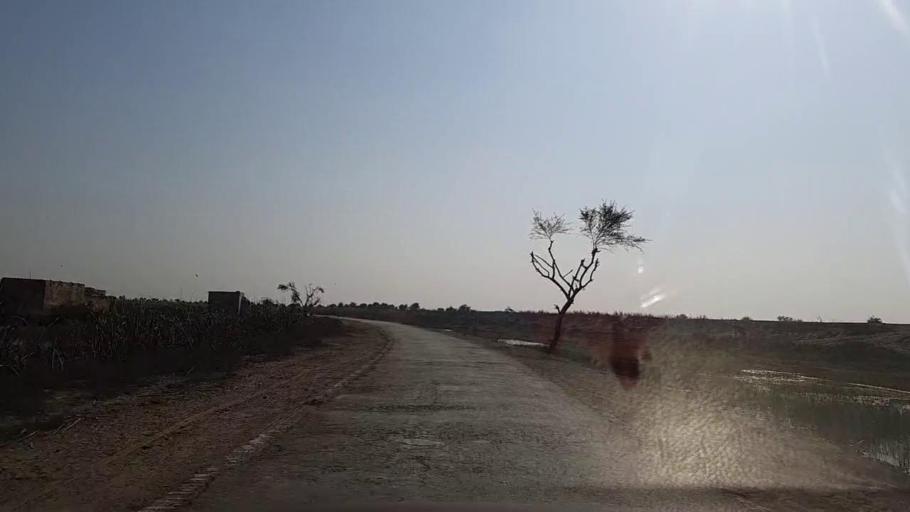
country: PK
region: Sindh
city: Sanghar
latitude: 25.9864
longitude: 69.0227
